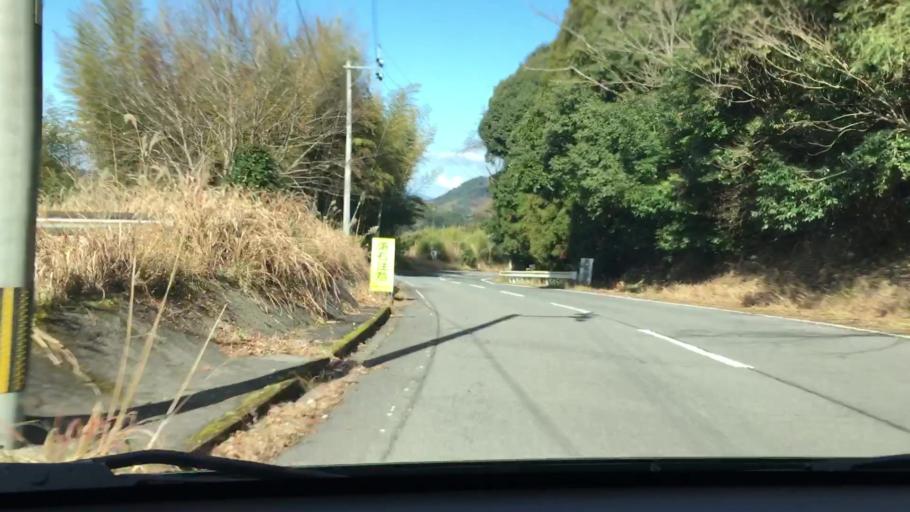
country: JP
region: Kagoshima
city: Ijuin
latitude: 31.7222
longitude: 130.4164
